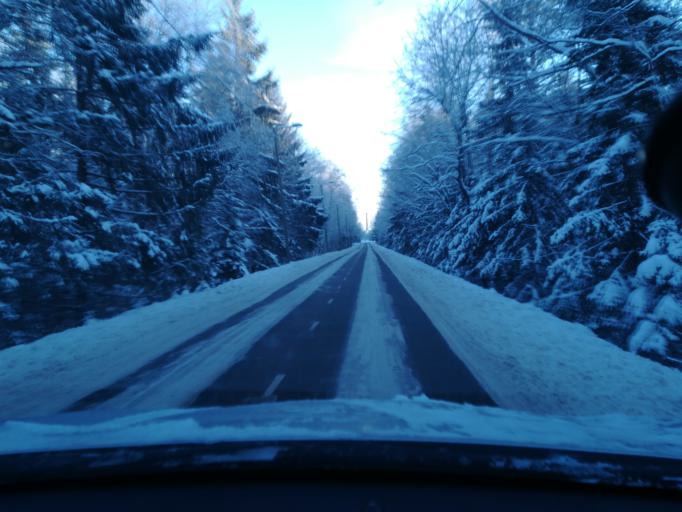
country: EE
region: Harju
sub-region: Saue vald
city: Laagri
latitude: 59.3887
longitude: 24.6202
